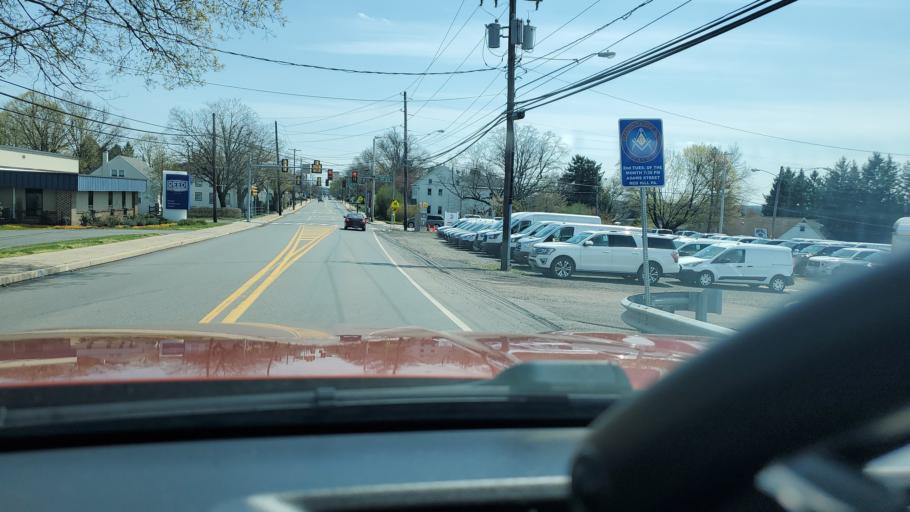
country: US
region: Pennsylvania
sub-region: Montgomery County
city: Pennsburg
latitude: 40.3854
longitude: -75.4885
